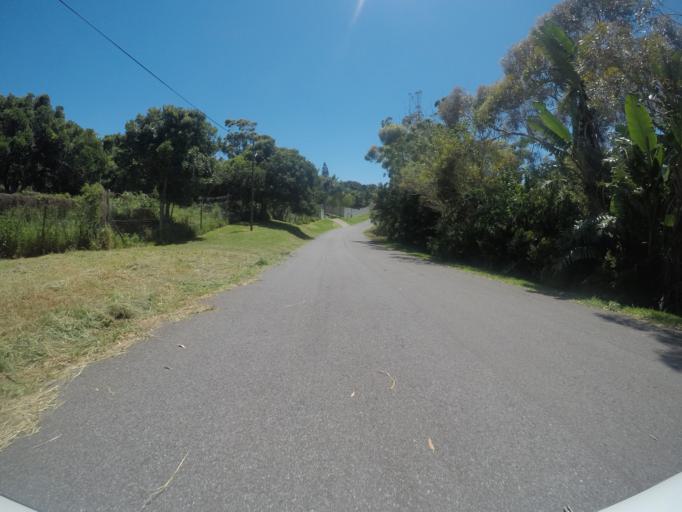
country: ZA
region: Eastern Cape
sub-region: Buffalo City Metropolitan Municipality
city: East London
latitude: -32.9355
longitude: 28.0044
